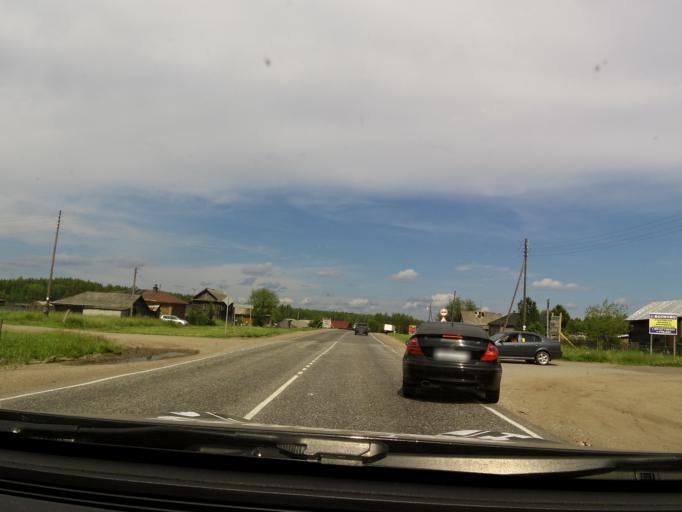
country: RU
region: Kirov
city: Vakhrushi
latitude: 58.6718
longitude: 49.9437
